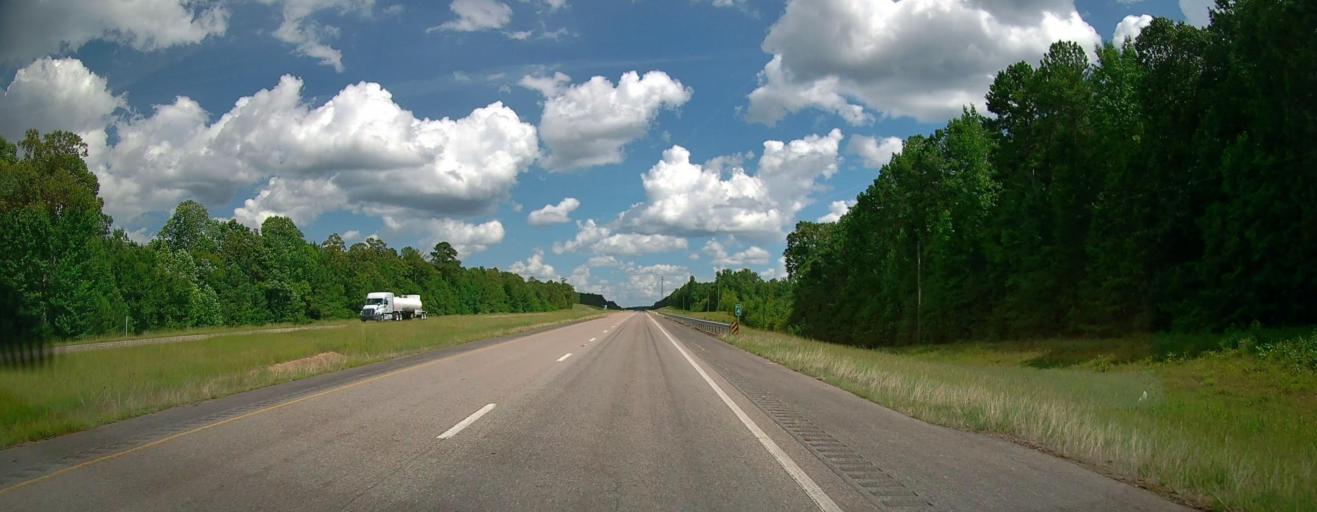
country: US
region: Mississippi
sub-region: Lowndes County
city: New Hope
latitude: 33.4605
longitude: -88.2247
